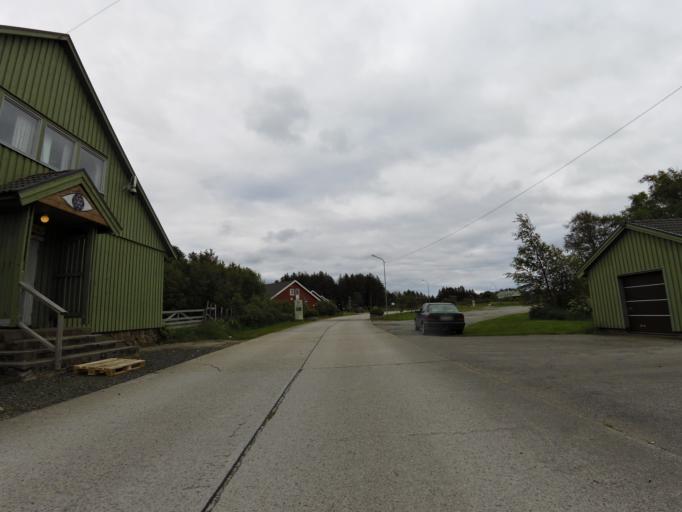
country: NO
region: Vest-Agder
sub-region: Farsund
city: Vestbygd
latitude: 58.1164
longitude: 6.6100
